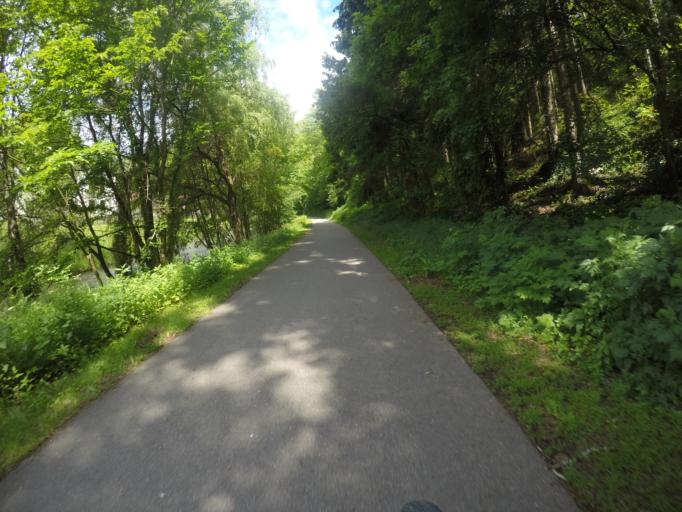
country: DE
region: Baden-Wuerttemberg
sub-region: Karlsruhe Region
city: Wildberg
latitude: 48.6228
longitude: 8.7522
